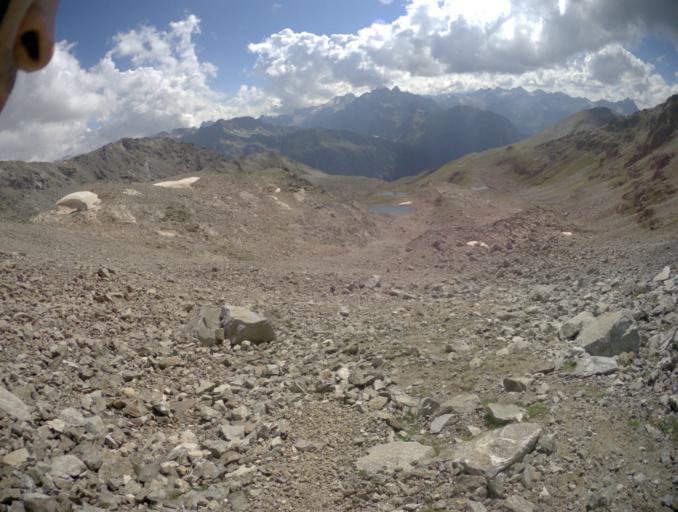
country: RU
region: Karachayevo-Cherkesiya
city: Uchkulan
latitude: 43.3177
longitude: 42.0763
